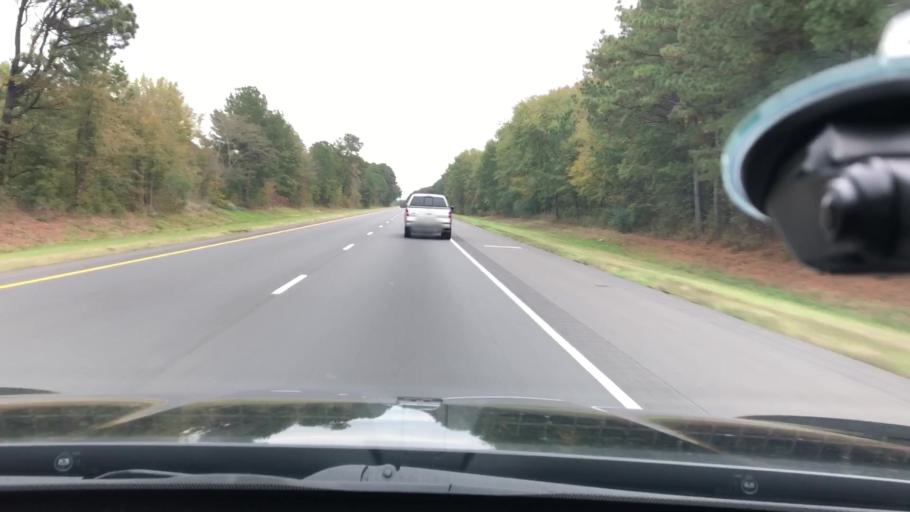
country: US
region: Arkansas
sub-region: Hempstead County
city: Hope
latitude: 33.7287
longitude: -93.5386
